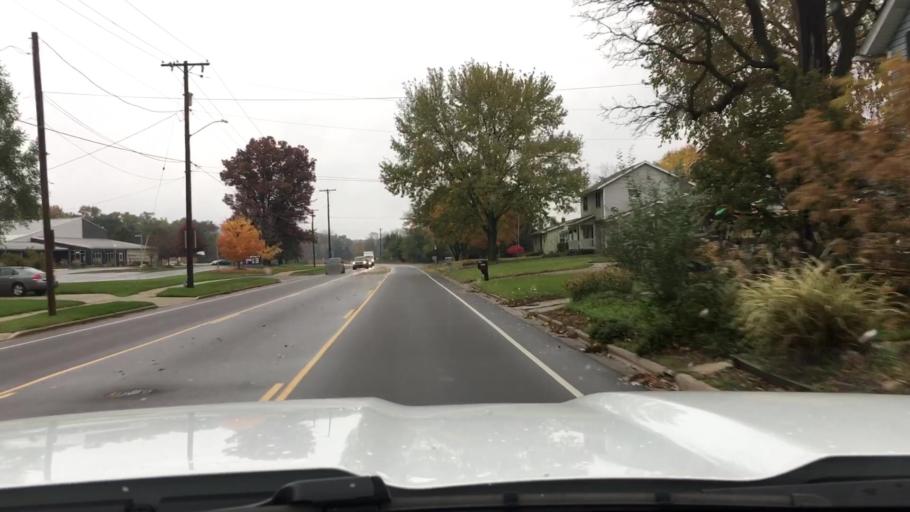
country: US
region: Michigan
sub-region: Kent County
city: Lowell
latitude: 42.9429
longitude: -85.3452
